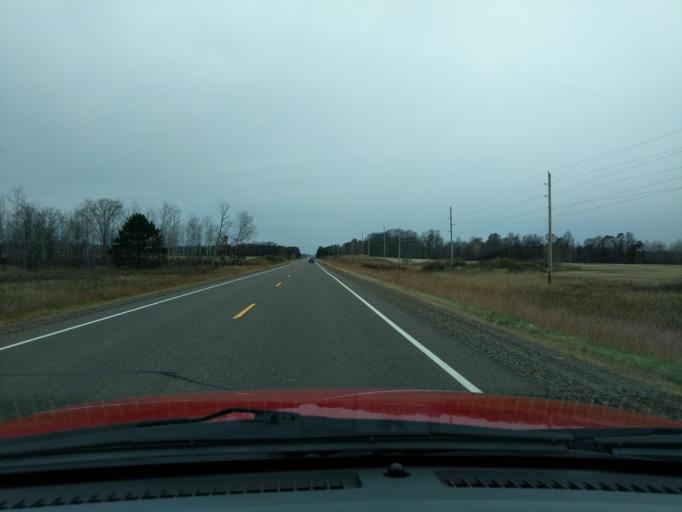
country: US
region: Wisconsin
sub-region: Washburn County
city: Shell Lake
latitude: 45.8154
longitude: -92.0784
